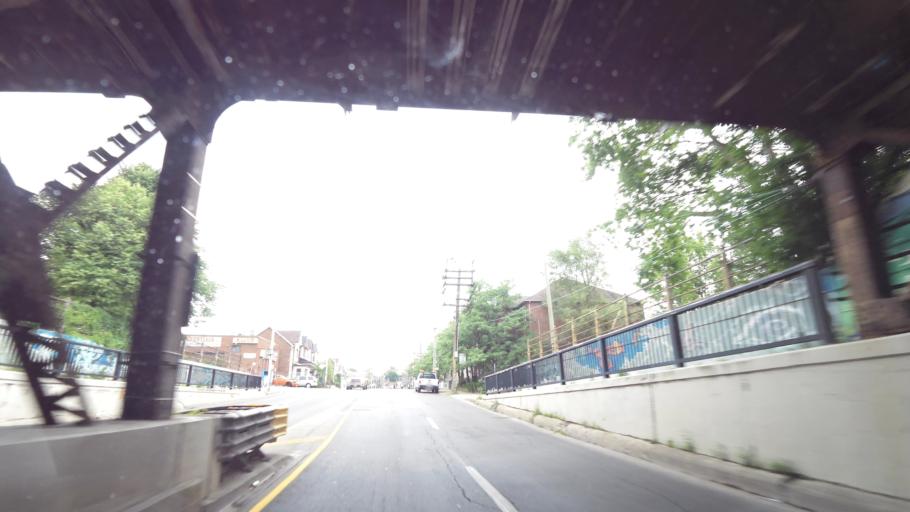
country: CA
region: Ontario
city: Toronto
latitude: 43.6710
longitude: -79.4295
